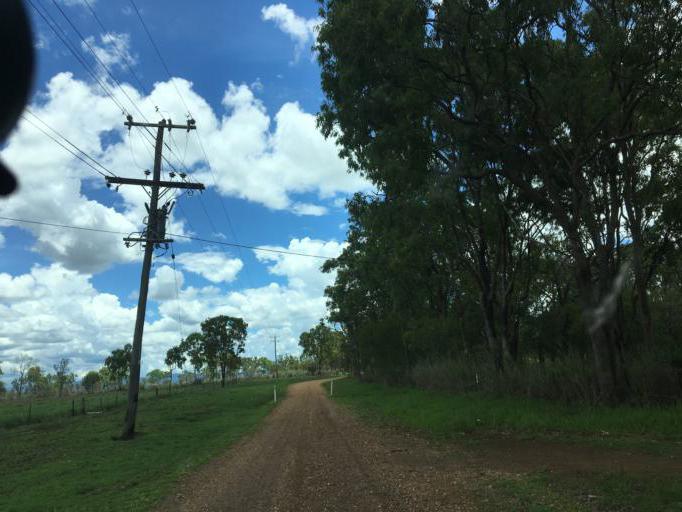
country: AU
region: Queensland
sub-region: Tablelands
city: Mareeba
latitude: -16.9920
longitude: 145.5220
